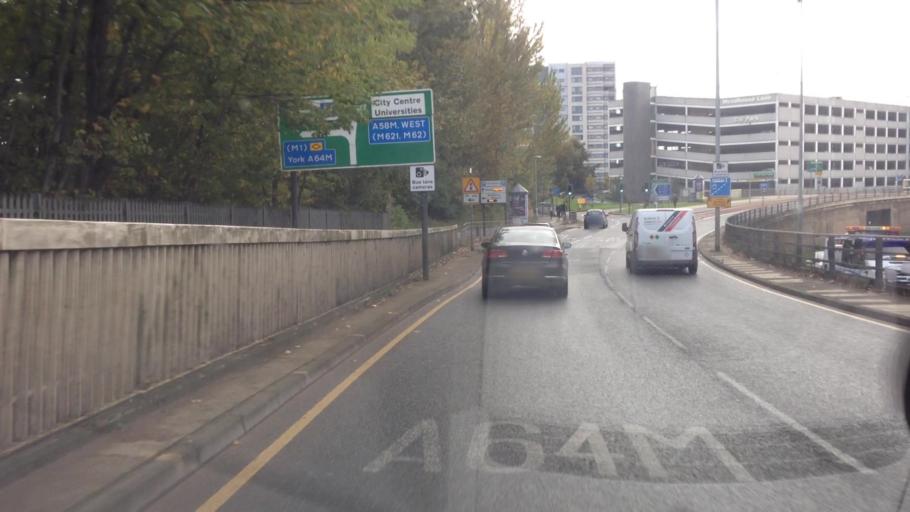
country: GB
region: England
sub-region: City and Borough of Leeds
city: Leeds
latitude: 53.8067
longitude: -1.5482
